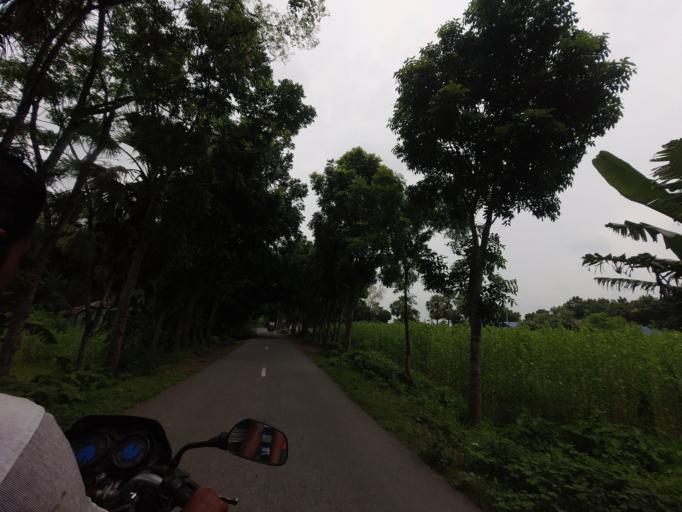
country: BD
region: Khulna
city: Kalia
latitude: 23.1081
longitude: 89.6469
